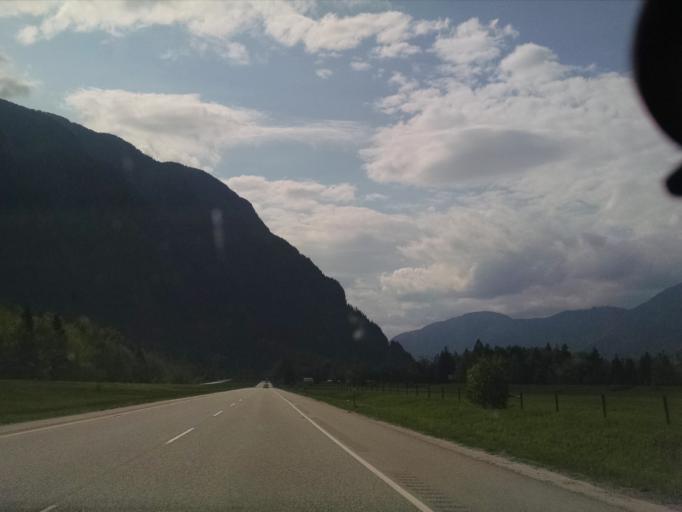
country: CA
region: British Columbia
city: Hope
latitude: 49.3638
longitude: -121.4955
